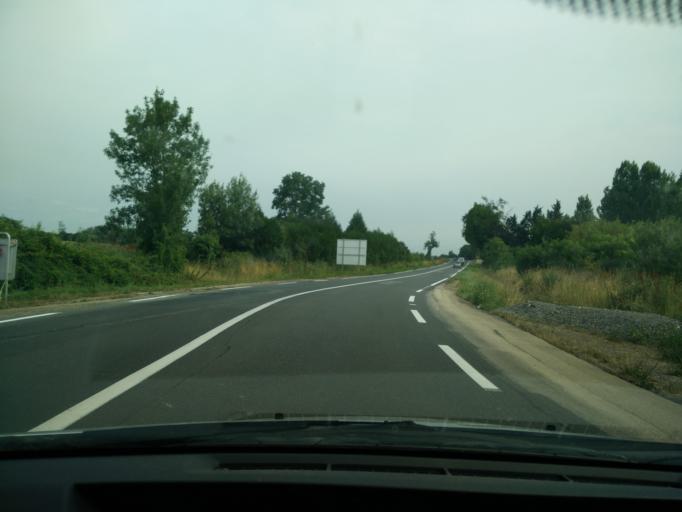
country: FR
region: Poitou-Charentes
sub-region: Departement des Deux-Sevres
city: Sainte-Verge
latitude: 47.0163
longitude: -0.1996
